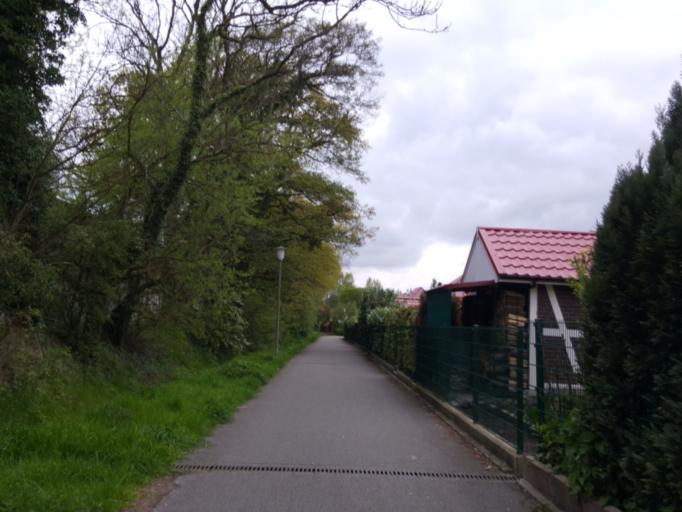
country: DE
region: Schleswig-Holstein
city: Oststeinbek
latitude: 53.5158
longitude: 10.1657
